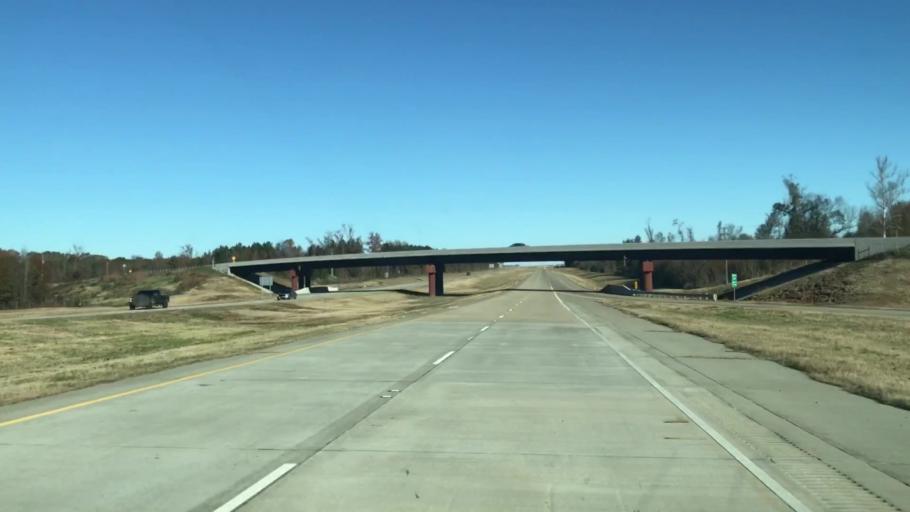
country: US
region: Louisiana
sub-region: Caddo Parish
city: Blanchard
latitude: 32.5990
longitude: -93.8321
